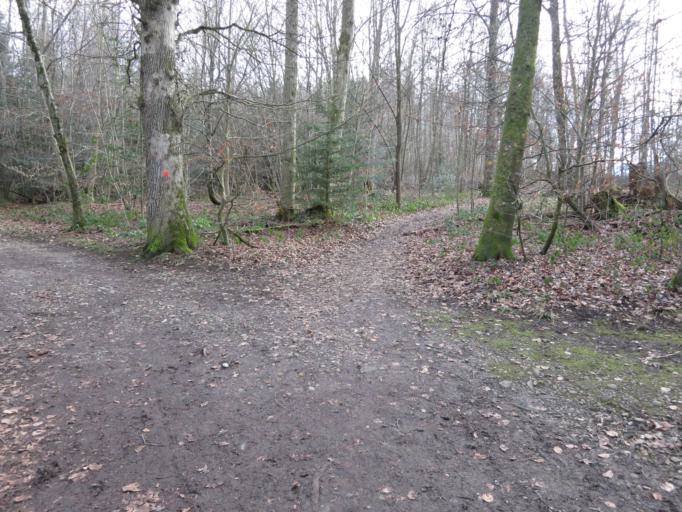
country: CH
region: Zurich
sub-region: Bezirk Meilen
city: Uerikon
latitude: 47.2391
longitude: 8.7666
